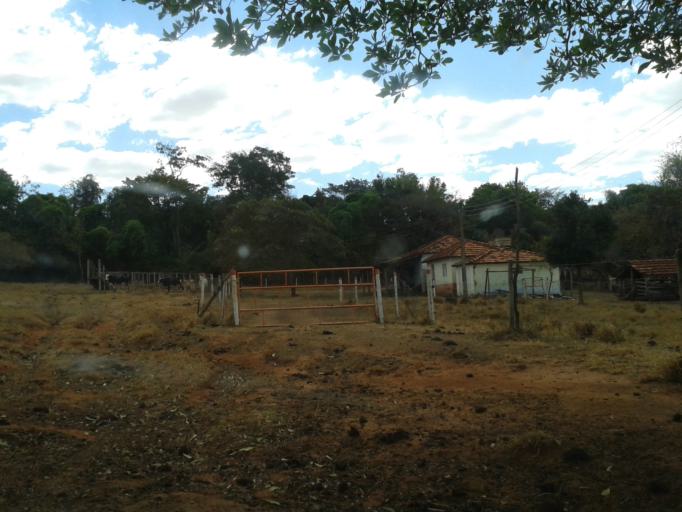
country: BR
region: Minas Gerais
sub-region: Centralina
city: Centralina
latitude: -18.7866
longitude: -49.1016
